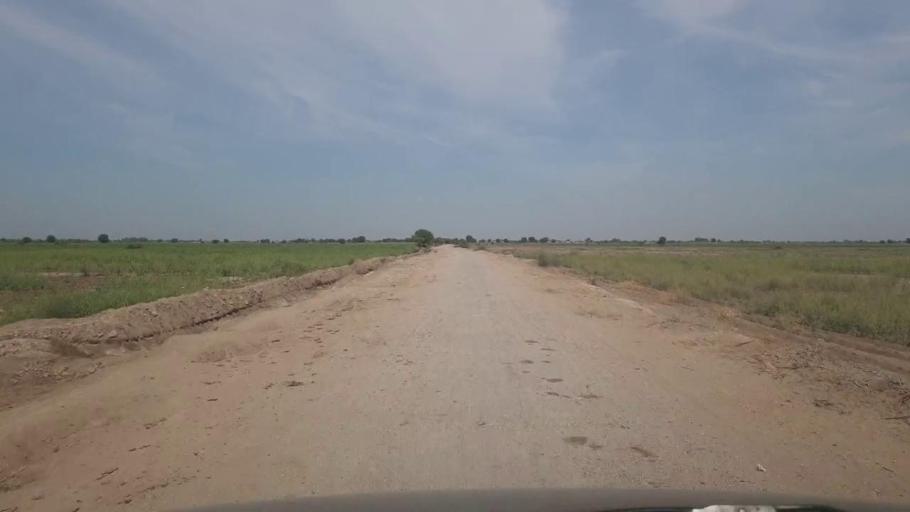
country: PK
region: Sindh
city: Kunri
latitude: 25.2340
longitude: 69.6259
